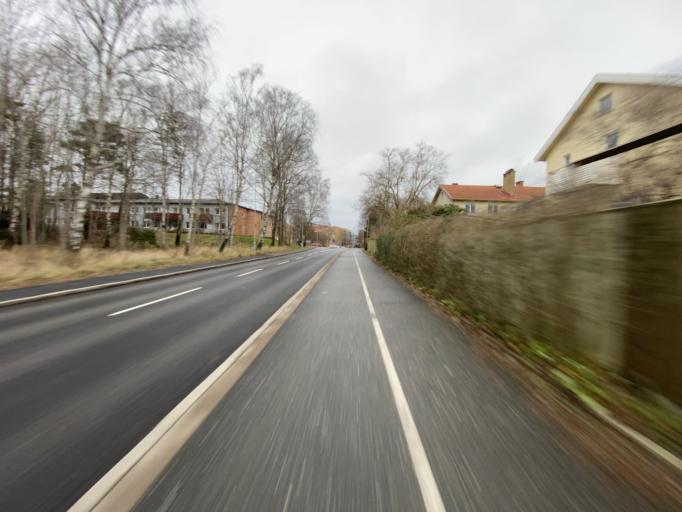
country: SE
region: Vaestra Goetaland
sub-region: Goteborg
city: Eriksbo
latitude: 57.7134
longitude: 12.0439
